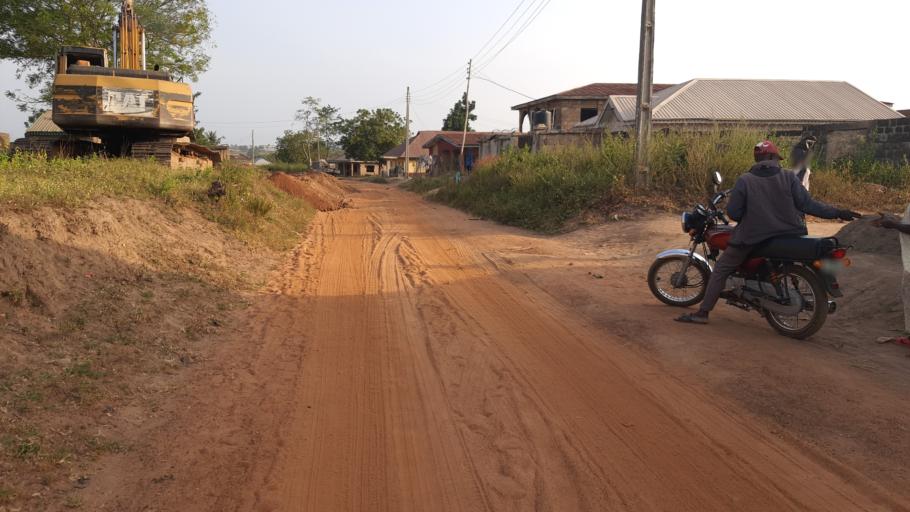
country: NG
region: Osun
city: Iwo
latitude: 7.6227
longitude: 4.1591
